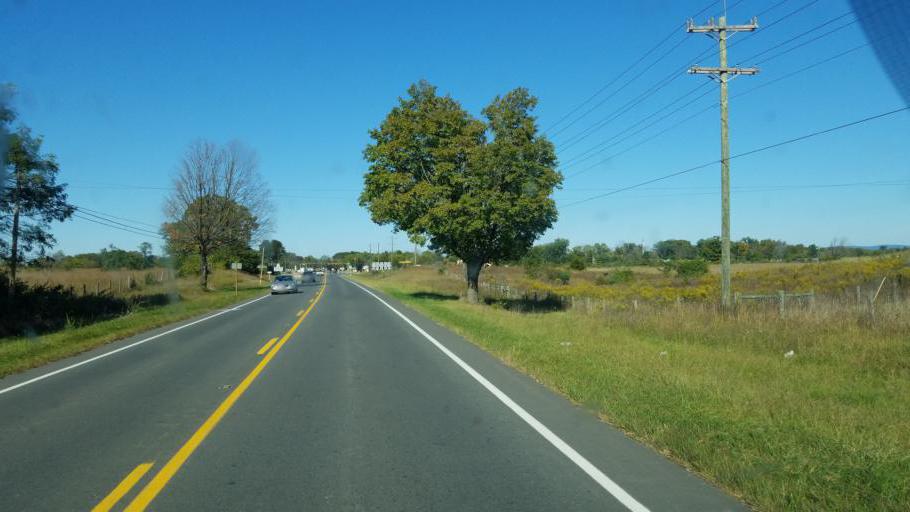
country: US
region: Virginia
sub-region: Warren County
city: Shenandoah Farms
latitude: 39.0785
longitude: -78.0871
